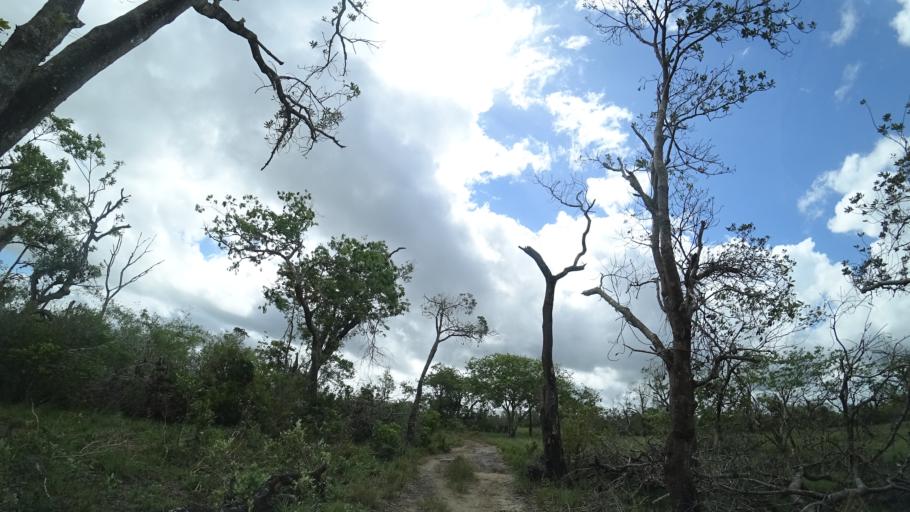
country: MZ
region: Sofala
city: Dondo
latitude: -19.5547
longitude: 35.1001
